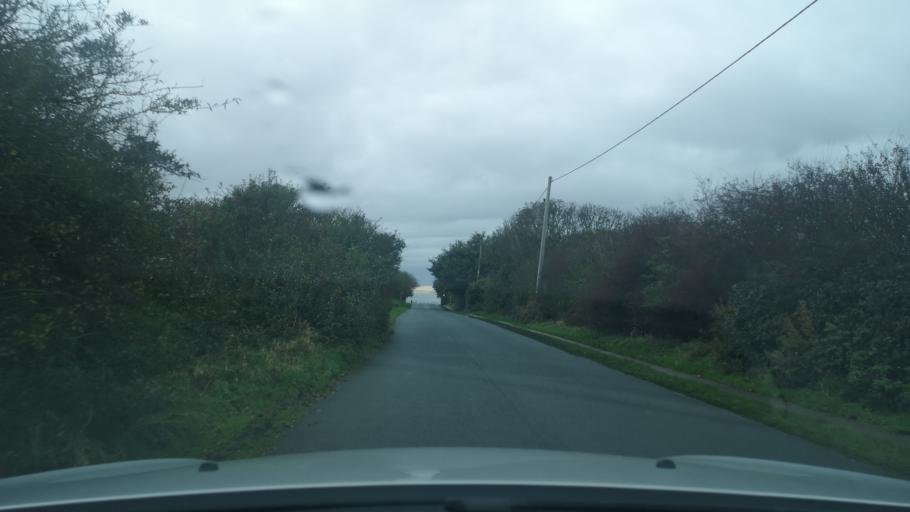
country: GB
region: England
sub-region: East Riding of Yorkshire
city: Easington
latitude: 53.6199
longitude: 0.1331
